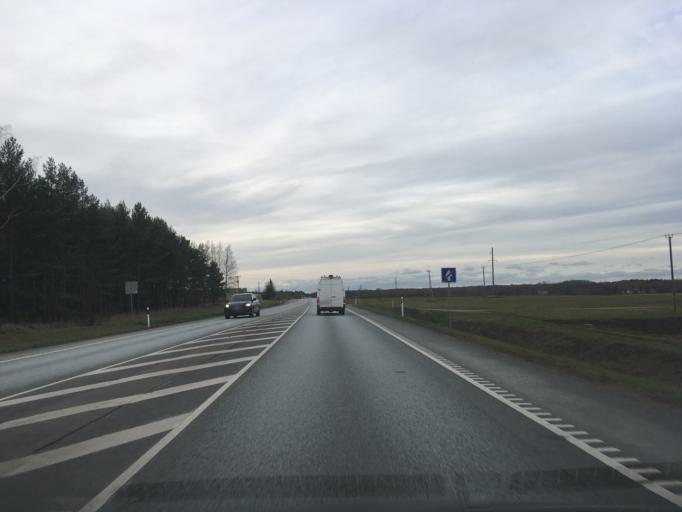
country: EE
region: Ida-Virumaa
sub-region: Kohtla-Jaerve linn
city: Kohtla-Jarve
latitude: 59.4080
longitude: 27.3181
